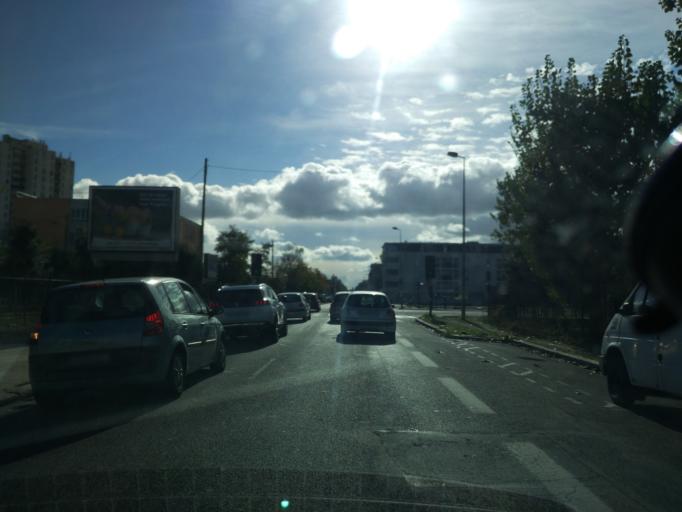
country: FR
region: Aquitaine
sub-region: Departement de la Gironde
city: Le Bouscat
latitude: 44.8659
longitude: -0.5650
